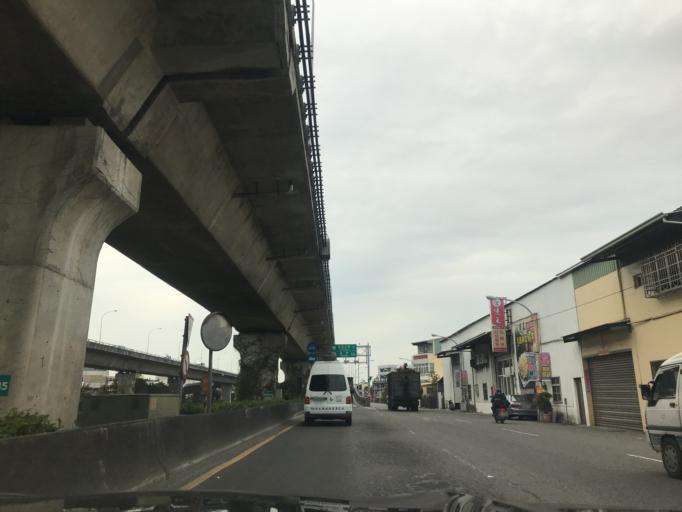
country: TW
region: Taiwan
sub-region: Nantou
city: Nantou
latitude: 23.9470
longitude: 120.5609
